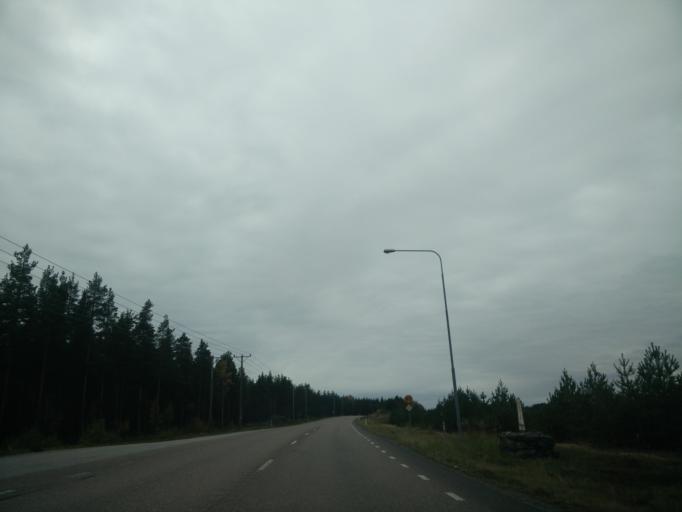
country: SE
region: Gaevleborg
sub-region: Gavle Kommun
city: Gavle
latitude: 60.7950
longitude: 17.2076
